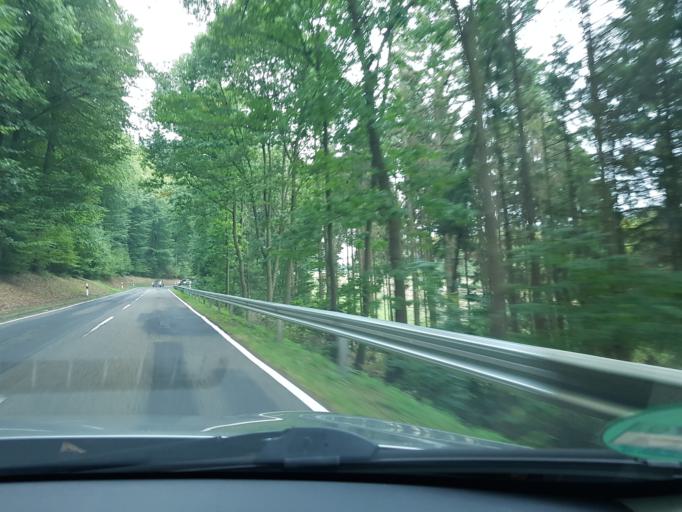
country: DE
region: Rheinland-Pfalz
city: Becheln
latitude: 50.3081
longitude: 7.7082
